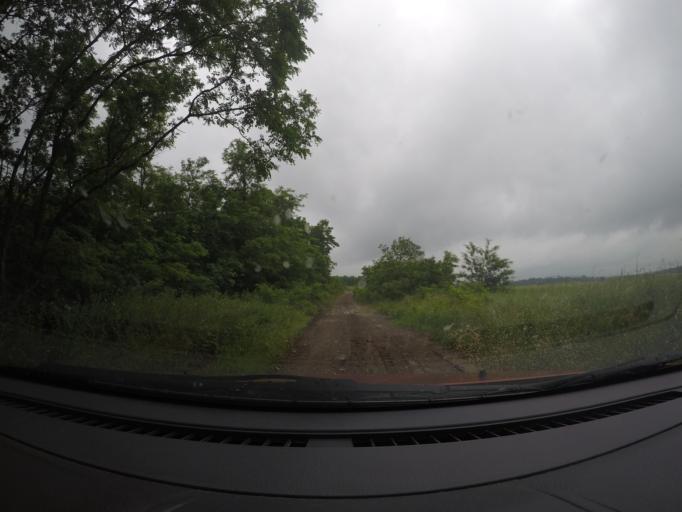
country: RS
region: Central Serbia
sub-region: Belgrade
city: Sopot
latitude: 44.5483
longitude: 20.5088
